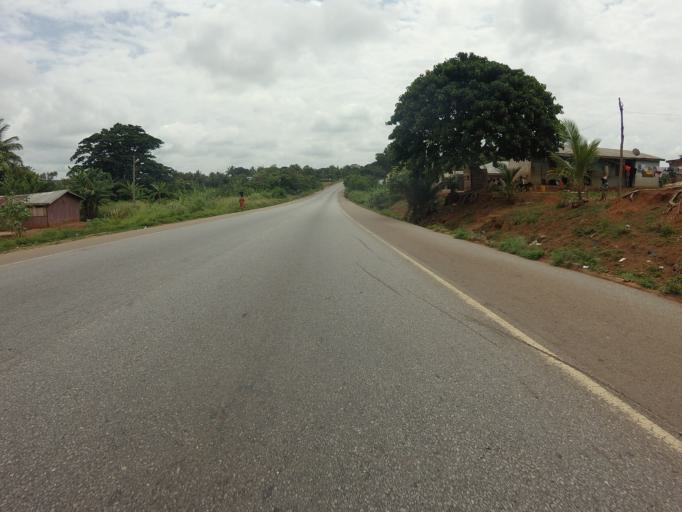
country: GH
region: Brong-Ahafo
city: Techiman
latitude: 7.4610
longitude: -1.9710
